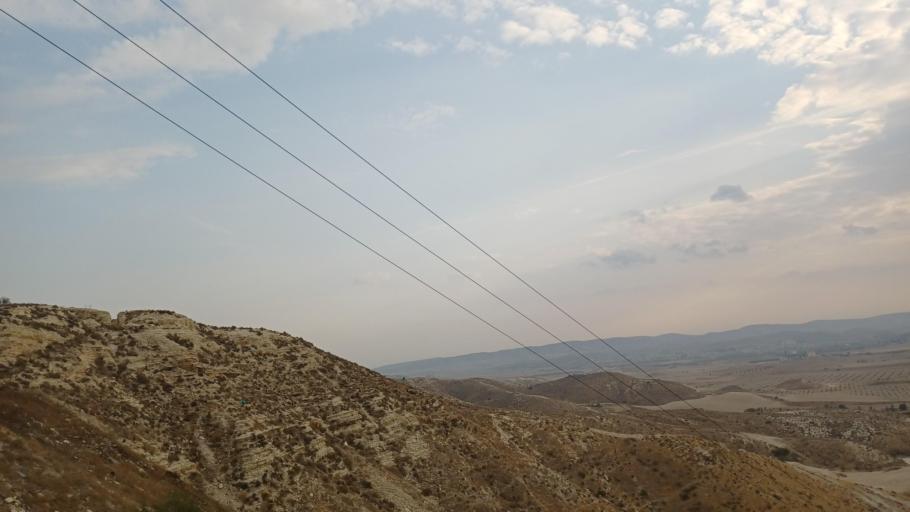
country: CY
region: Larnaka
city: Troulloi
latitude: 35.0283
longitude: 33.5748
